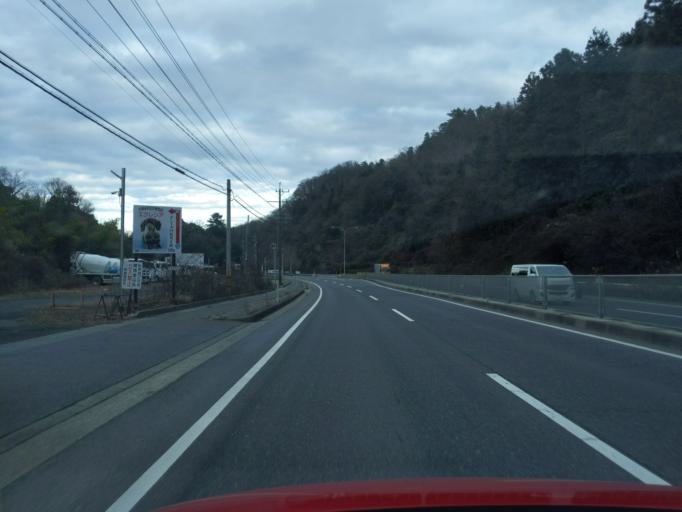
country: JP
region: Gifu
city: Tajimi
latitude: 35.3289
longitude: 137.0863
